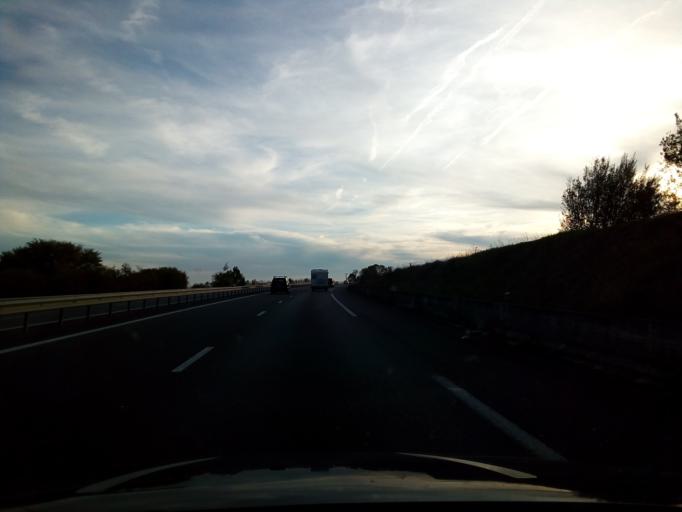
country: FR
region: Poitou-Charentes
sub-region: Departement de la Charente-Maritime
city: Montlieu-la-Garde
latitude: 45.2639
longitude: -0.2492
